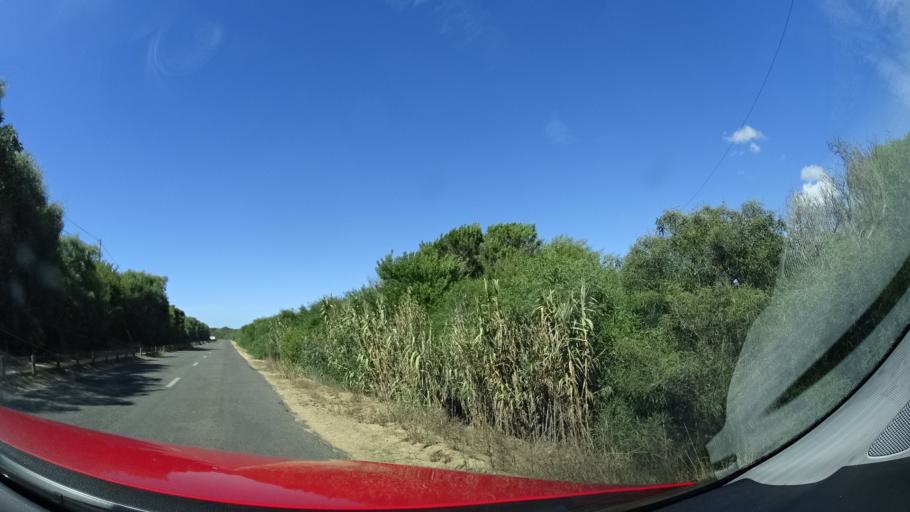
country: PT
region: Beja
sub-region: Odemira
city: Sao Teotonio
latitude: 37.5338
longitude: -8.7845
